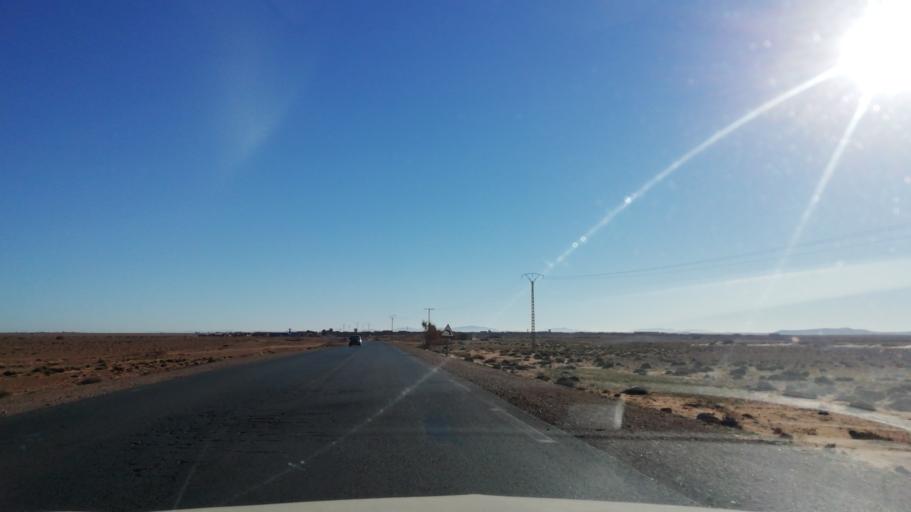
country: DZ
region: El Bayadh
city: El Bayadh
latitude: 33.8539
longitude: 0.6120
